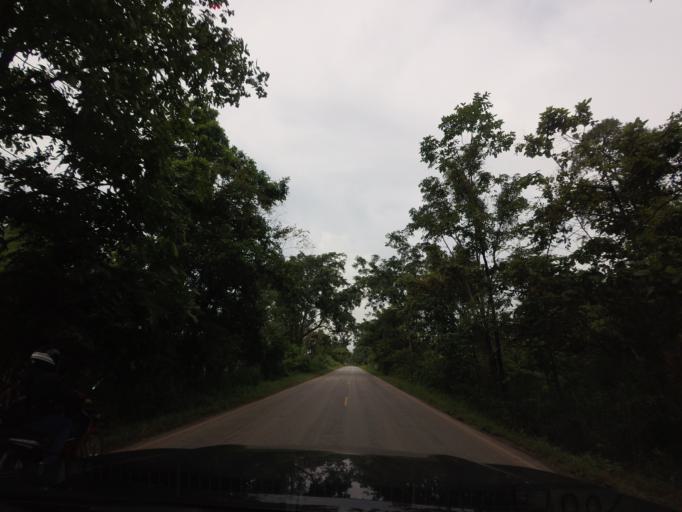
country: TH
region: Changwat Nong Bua Lamphu
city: Suwannakhuha
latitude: 17.4840
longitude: 102.3657
